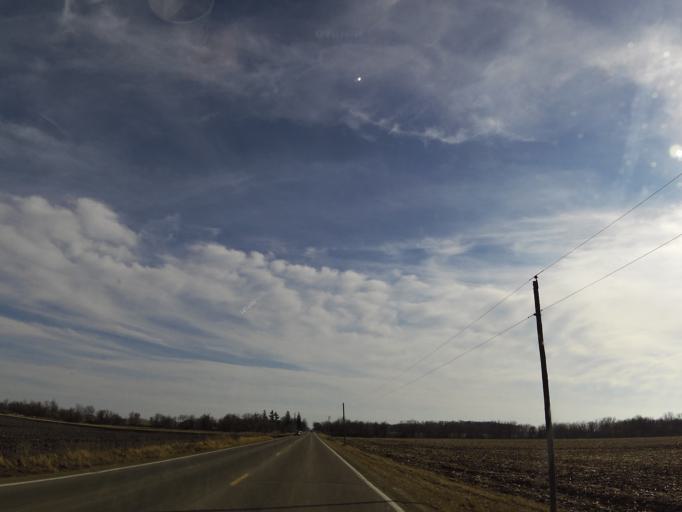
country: US
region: Minnesota
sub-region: Rice County
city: Northfield
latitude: 44.5259
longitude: -93.2003
